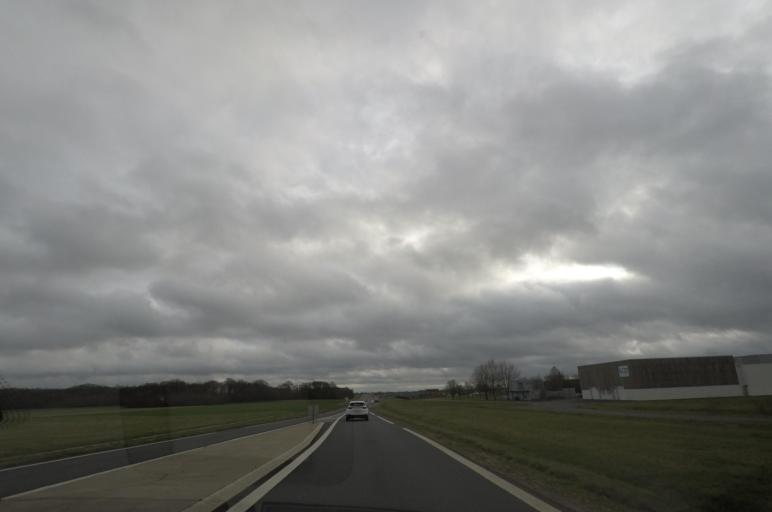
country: FR
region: Centre
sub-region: Departement du Loir-et-Cher
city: Saint-Sulpice-de-Pommeray
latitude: 47.6829
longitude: 1.2094
